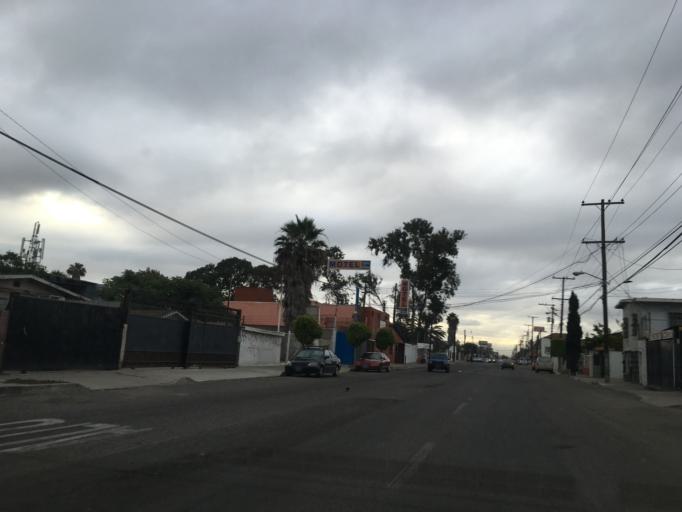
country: MX
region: Baja California
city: Tijuana
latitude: 32.5388
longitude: -117.0598
